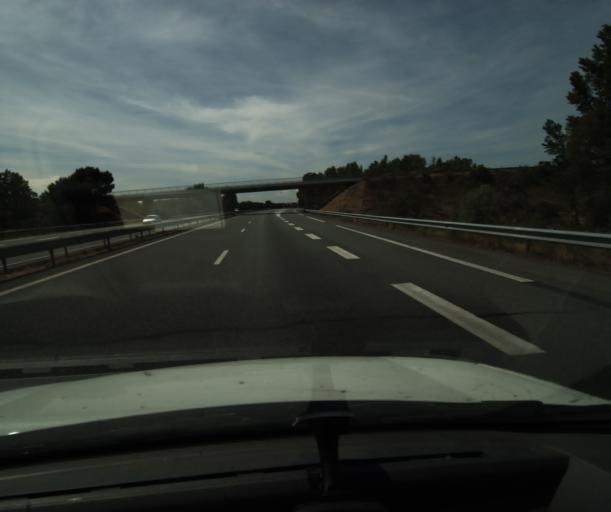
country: FR
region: Languedoc-Roussillon
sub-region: Departement de l'Aude
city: Bram
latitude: 43.2277
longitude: 2.1199
